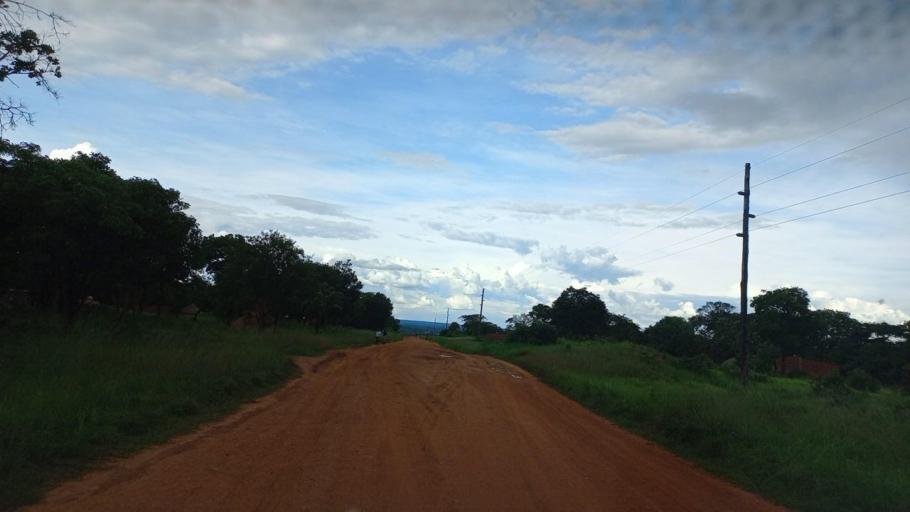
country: ZM
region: North-Western
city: Mwinilunga
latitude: -11.7667
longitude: 24.4111
